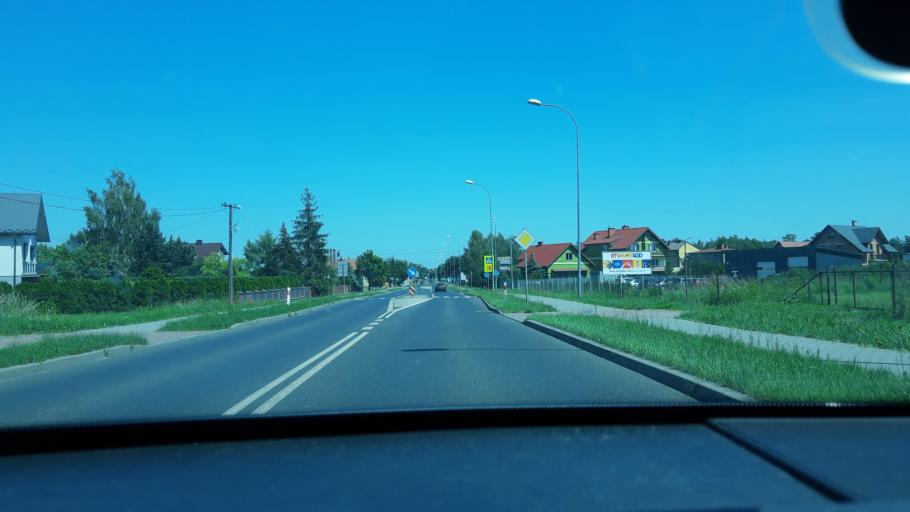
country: PL
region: Lodz Voivodeship
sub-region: Powiat zdunskowolski
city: Zdunska Wola
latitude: 51.6078
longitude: 18.9069
